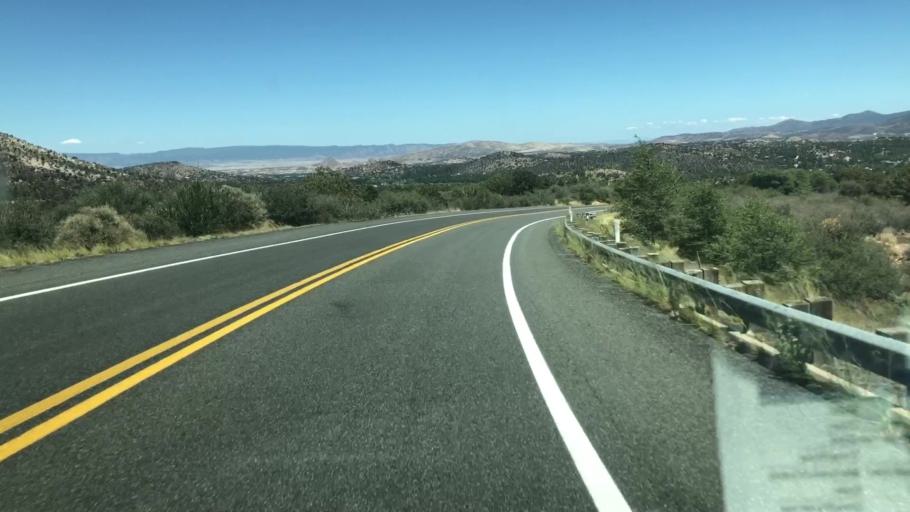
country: US
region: Arizona
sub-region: Yavapai County
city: Prescott
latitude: 34.5821
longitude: -112.5434
